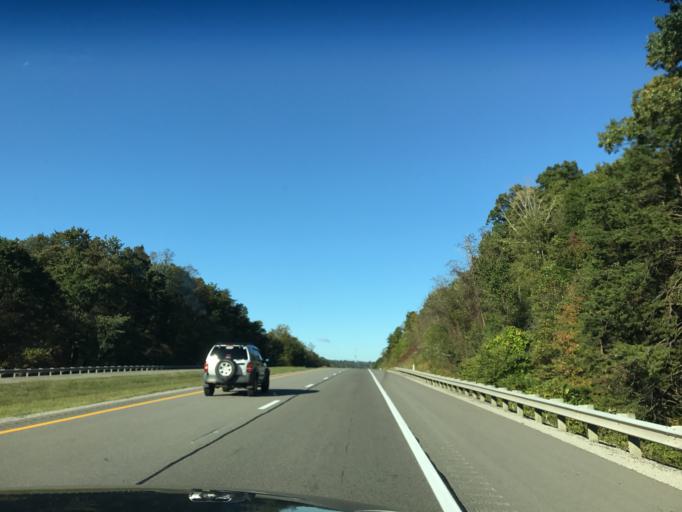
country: US
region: West Virginia
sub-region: Wood County
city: Mineral Wells
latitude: 39.2425
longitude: -81.4148
